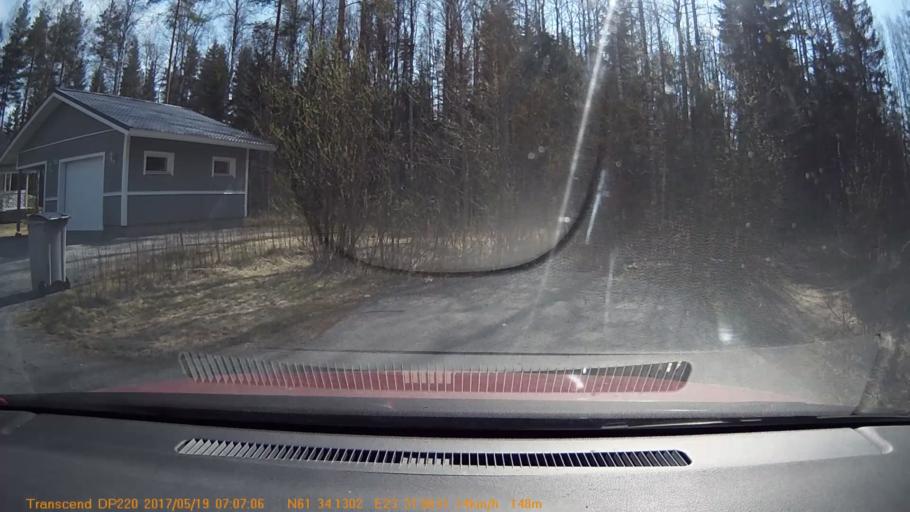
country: FI
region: Pirkanmaa
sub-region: Tampere
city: Yloejaervi
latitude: 61.5688
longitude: 23.5311
